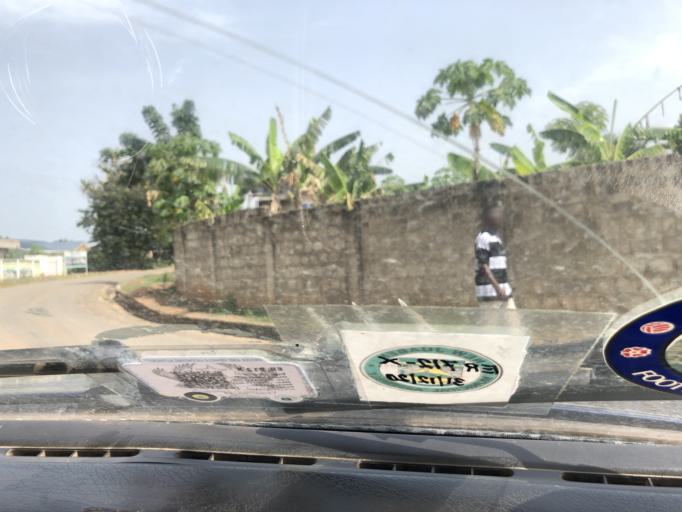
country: GH
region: Eastern
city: Koforidua
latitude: 6.0931
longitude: -0.2728
